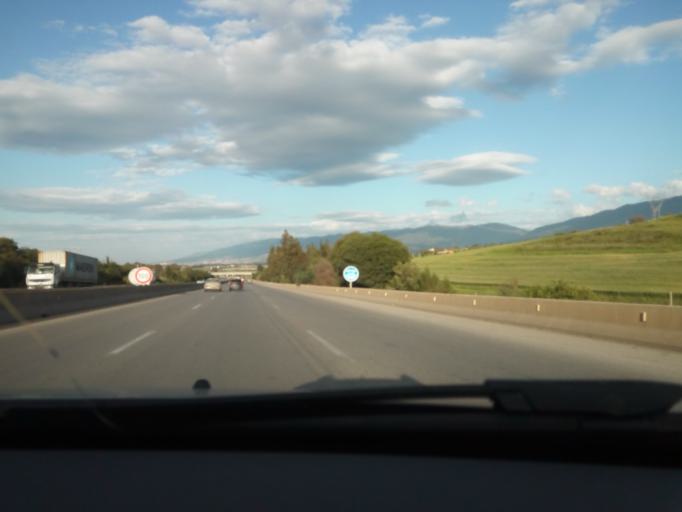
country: DZ
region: Tipaza
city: El Affroun
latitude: 36.4460
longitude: 2.6322
